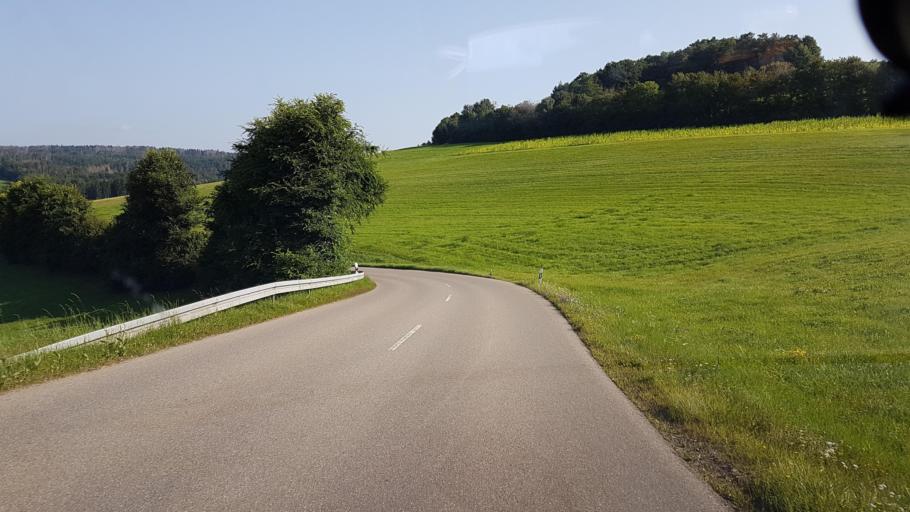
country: DE
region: Baden-Wuerttemberg
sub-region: Freiburg Region
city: Gorwihl
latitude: 47.6263
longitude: 8.1139
